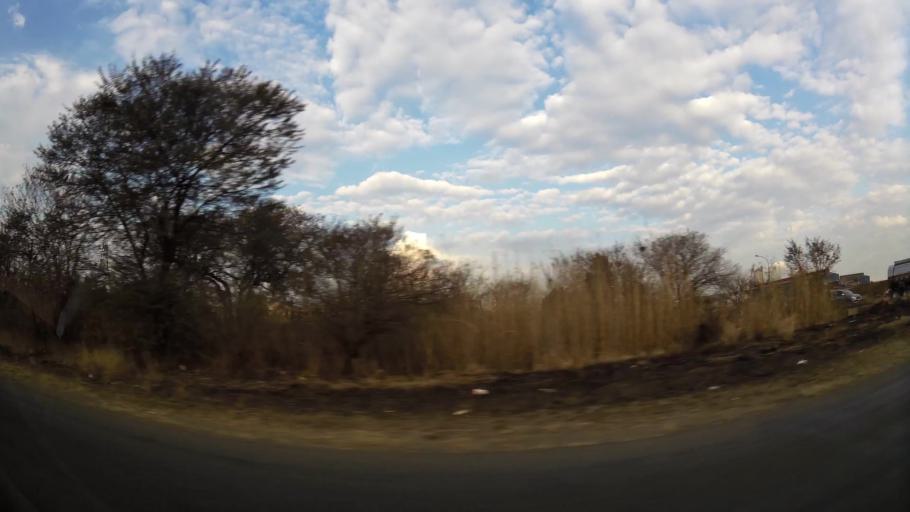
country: ZA
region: Gauteng
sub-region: Sedibeng District Municipality
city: Vanderbijlpark
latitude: -26.6660
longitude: 27.7961
